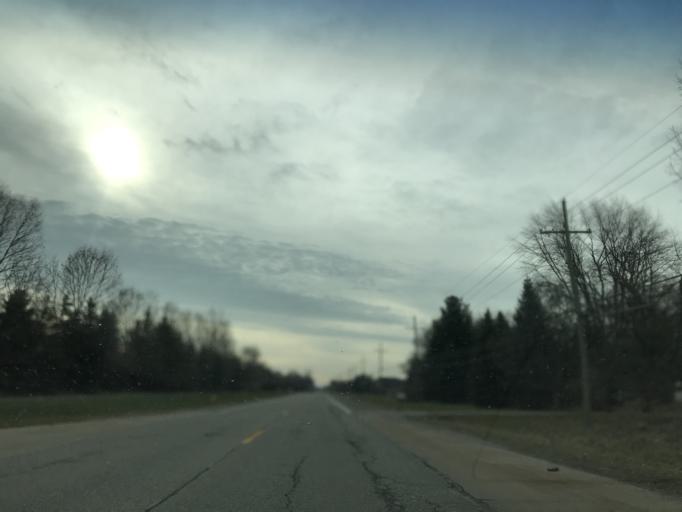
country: US
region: Michigan
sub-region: Macomb County
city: Mount Clemens
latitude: 42.6566
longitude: -82.8973
